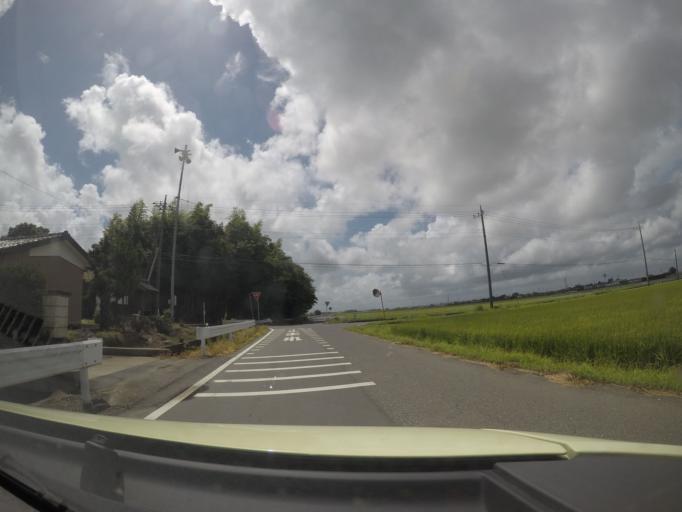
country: JP
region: Ibaraki
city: Mitsukaido
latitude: 36.0491
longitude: 140.0105
